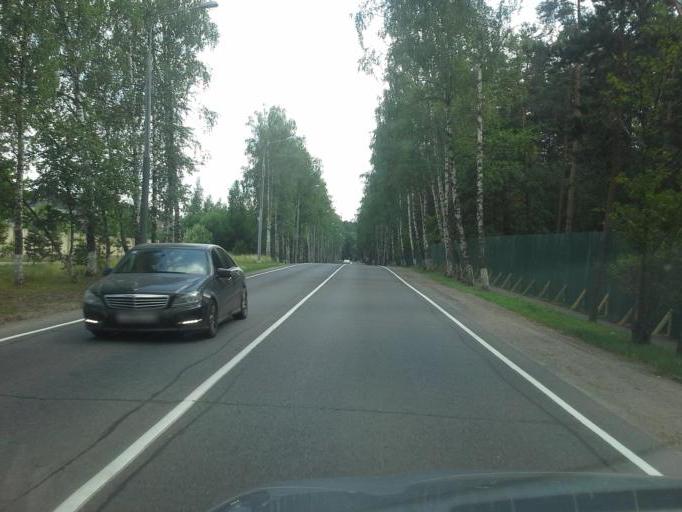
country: RU
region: Moskovskaya
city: Barvikha
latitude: 55.7351
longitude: 37.2717
